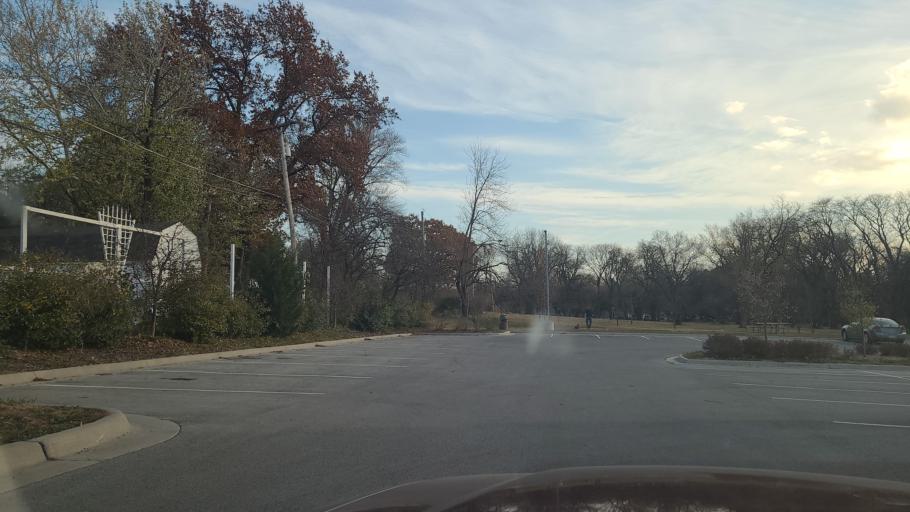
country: US
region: Kansas
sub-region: Douglas County
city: Lawrence
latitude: 38.9559
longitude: -95.2201
